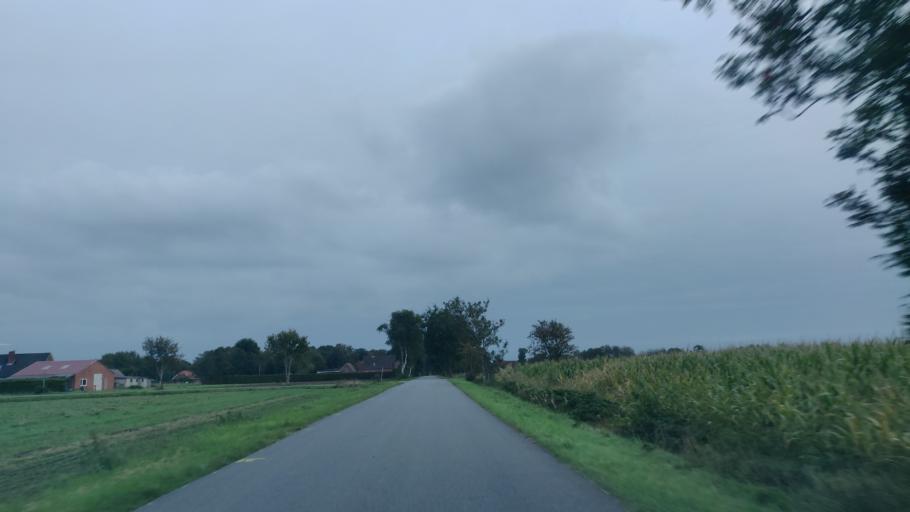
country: DE
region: Lower Saxony
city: Aurich
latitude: 53.4967
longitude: 7.4364
